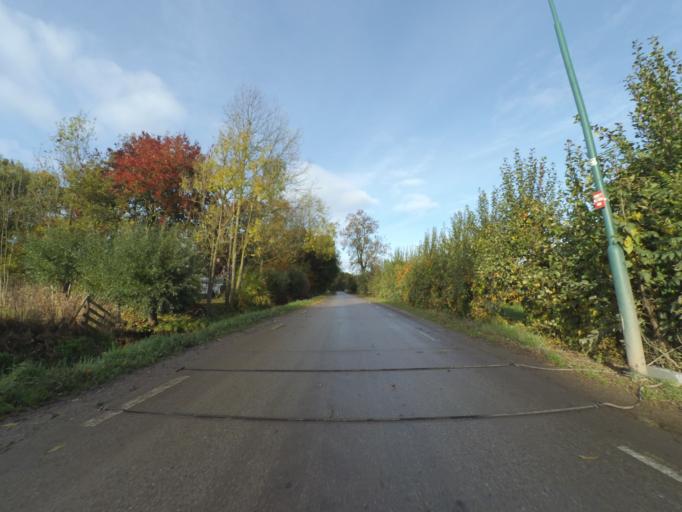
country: NL
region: Utrecht
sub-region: Gemeente Wijk bij Duurstede
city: Wijk bij Duurstede
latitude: 51.9800
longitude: 5.3049
